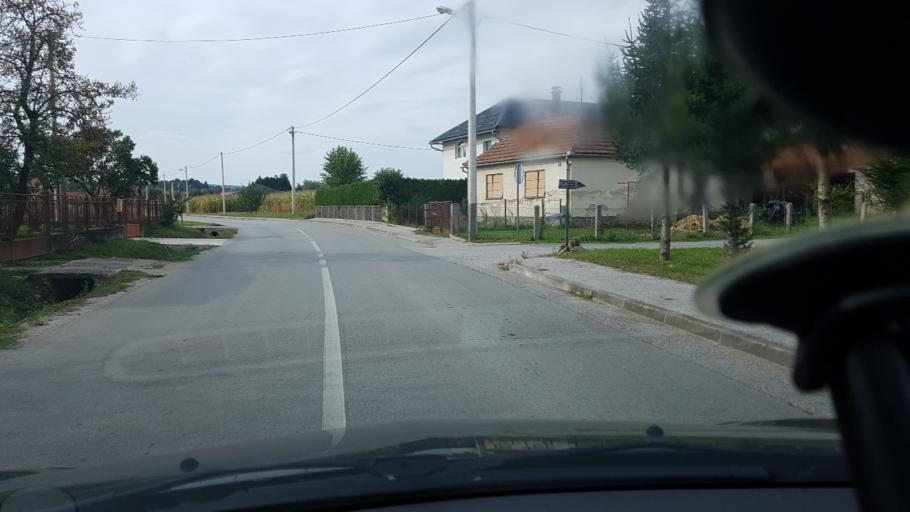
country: HR
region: Varazdinska
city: Ivanec
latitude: 46.2275
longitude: 16.1725
